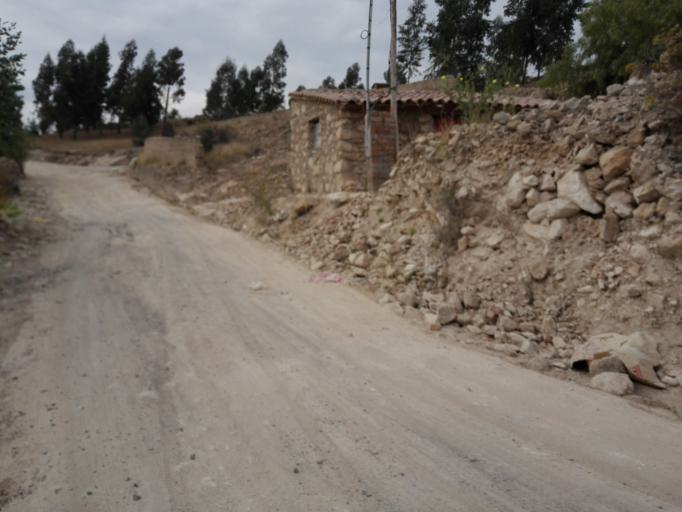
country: PE
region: Ayacucho
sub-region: Provincia de Huamanga
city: Ayacucho
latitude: -13.1491
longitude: -74.2374
